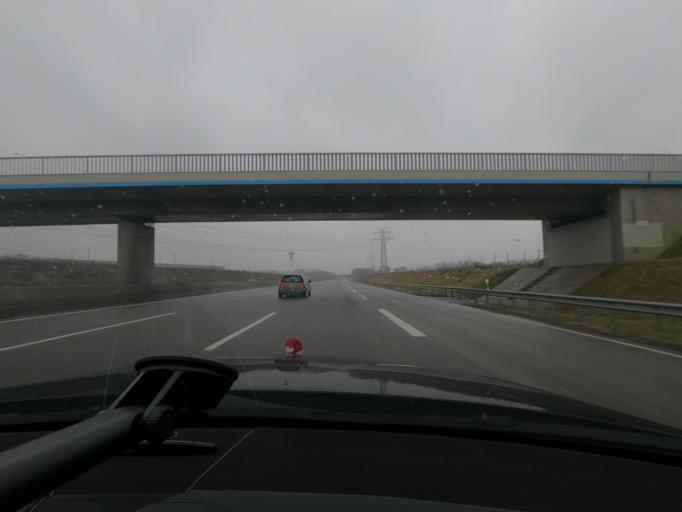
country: DE
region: Schleswig-Holstein
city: Nutzen
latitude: 53.8522
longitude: 9.9385
